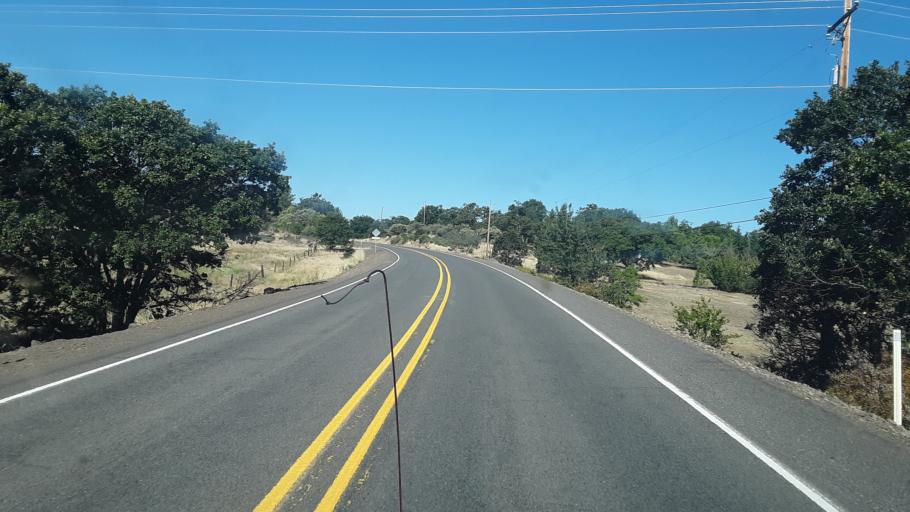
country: US
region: Oregon
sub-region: Jackson County
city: Eagle Point
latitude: 42.5258
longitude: -122.8468
